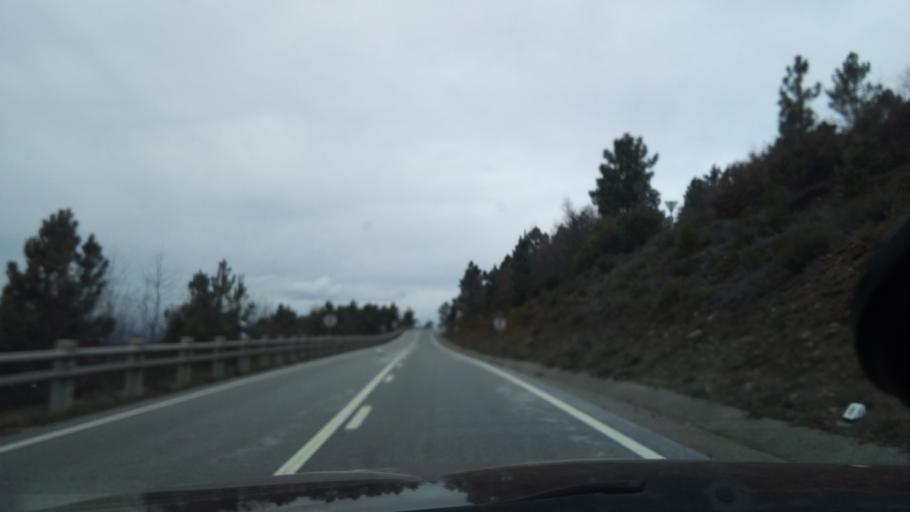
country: PT
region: Guarda
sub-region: Seia
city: Seia
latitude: 40.3456
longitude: -7.7132
